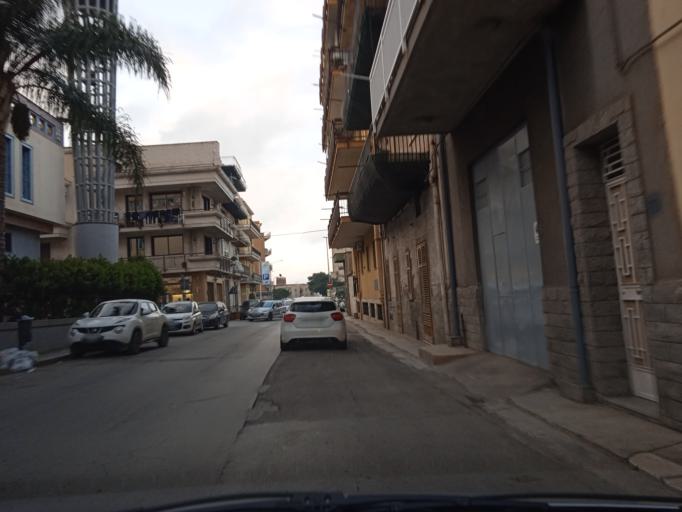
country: IT
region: Sicily
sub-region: Palermo
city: Villabate
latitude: 38.0800
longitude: 13.4365
